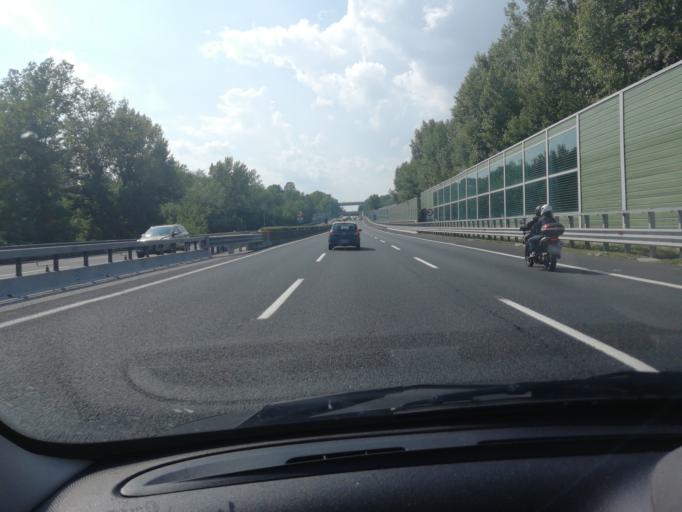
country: IT
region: Latium
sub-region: Provincia di Frosinone
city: Arnara
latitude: 41.5675
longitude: 13.3899
